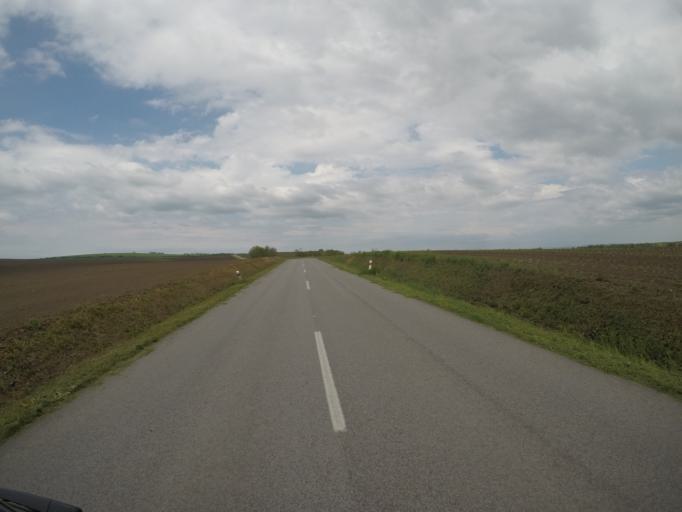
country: SK
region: Nitriansky
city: Zeliezovce
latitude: 48.0351
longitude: 18.8028
